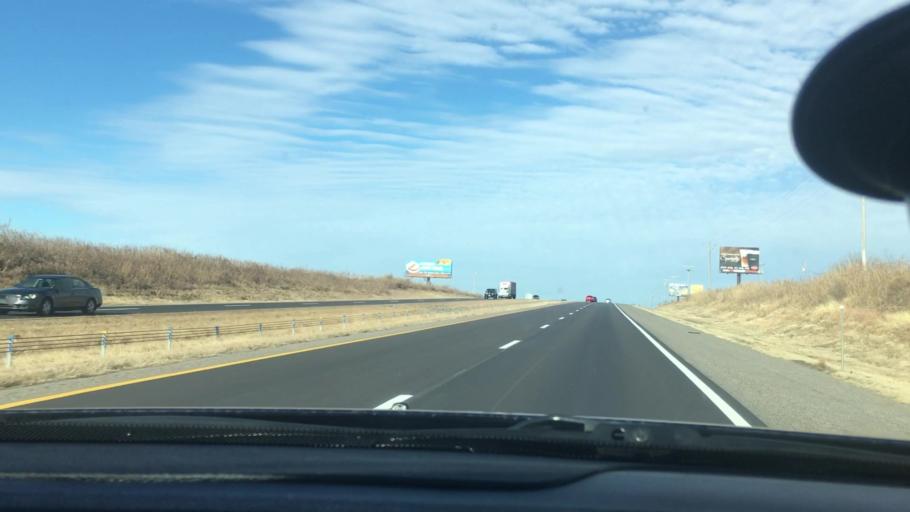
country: US
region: Oklahoma
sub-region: Cleveland County
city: Noble
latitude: 35.0901
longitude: -97.4182
